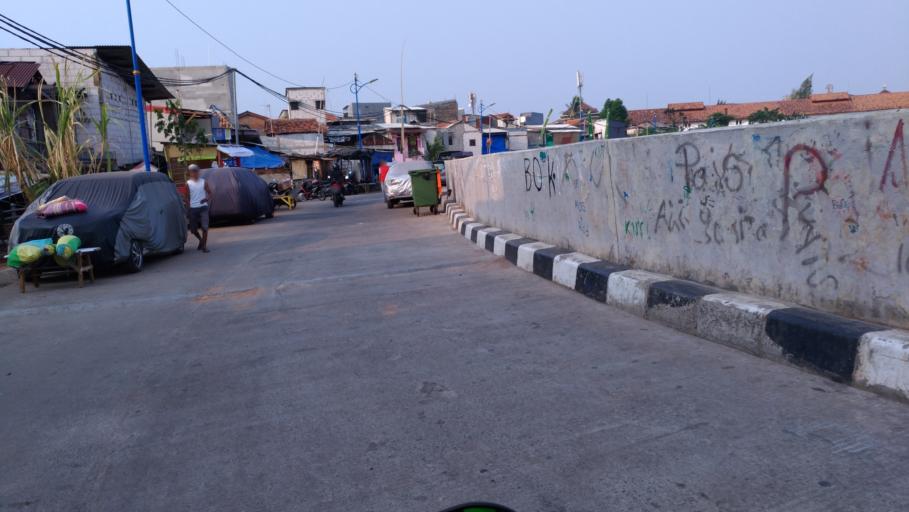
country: ID
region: Jakarta Raya
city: Jakarta
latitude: -6.2199
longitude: 106.8616
